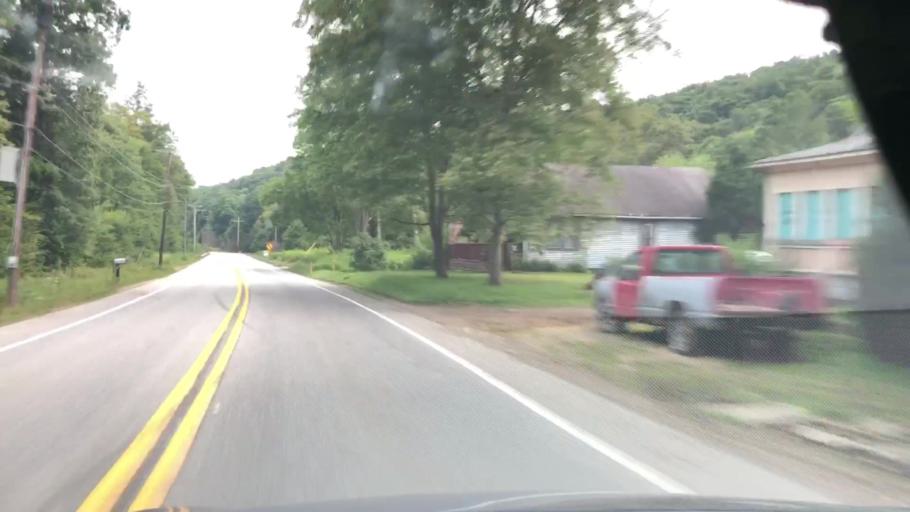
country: US
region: Pennsylvania
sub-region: Venango County
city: Hasson Heights
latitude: 41.4948
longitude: -79.7004
